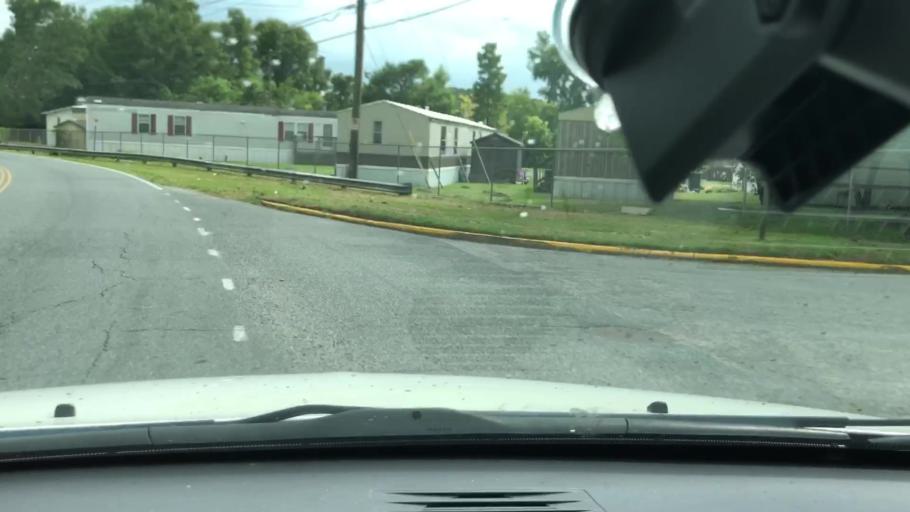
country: US
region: Virginia
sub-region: City of Chesapeake
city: Chesapeake
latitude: 36.7807
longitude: -76.2687
